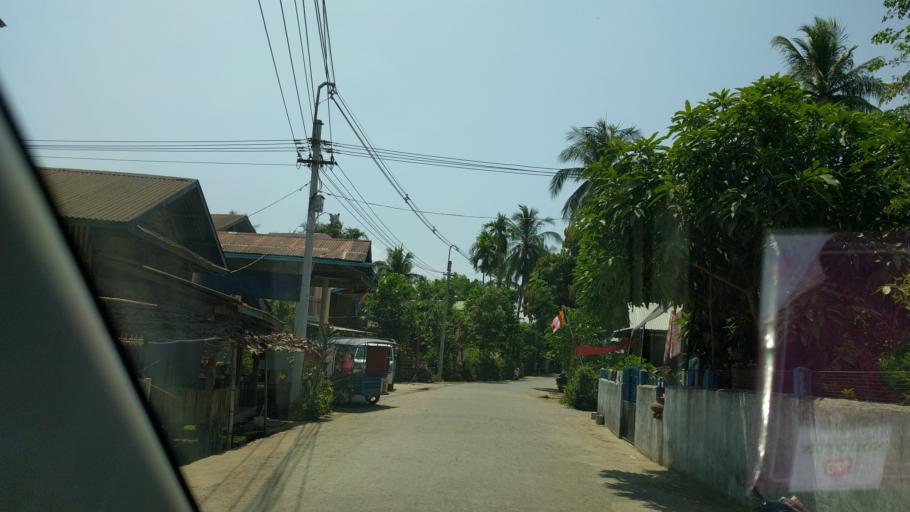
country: MM
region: Mon
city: Martaban
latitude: 16.6056
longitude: 97.6642
